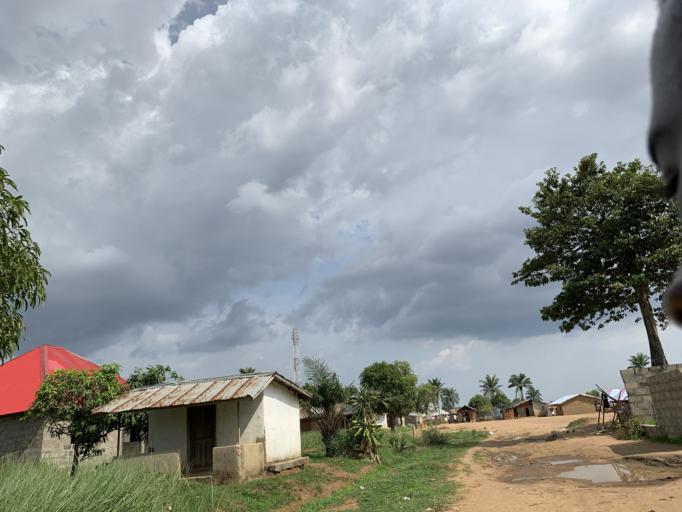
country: SL
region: Western Area
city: Waterloo
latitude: 8.3519
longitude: -13.0432
